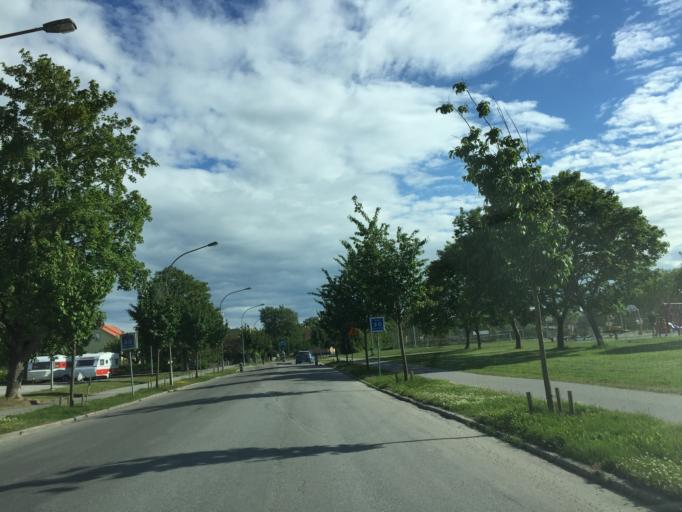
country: SE
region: OErebro
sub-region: Orebro Kommun
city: Orebro
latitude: 59.2874
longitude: 15.2278
